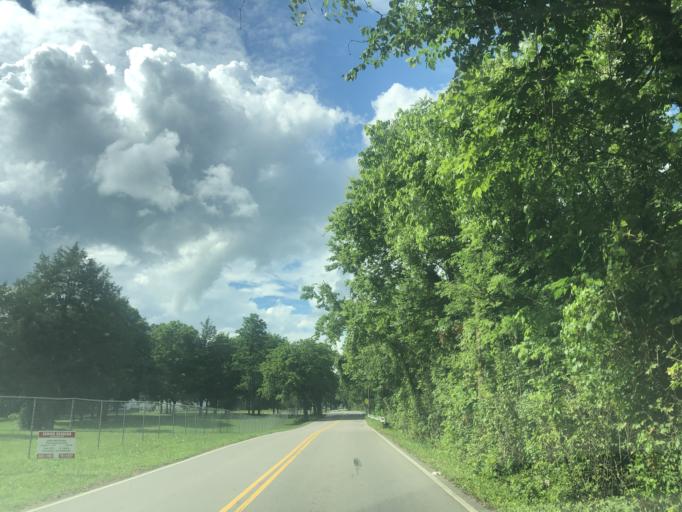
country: US
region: Tennessee
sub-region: Davidson County
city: Nashville
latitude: 36.2097
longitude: -86.8654
